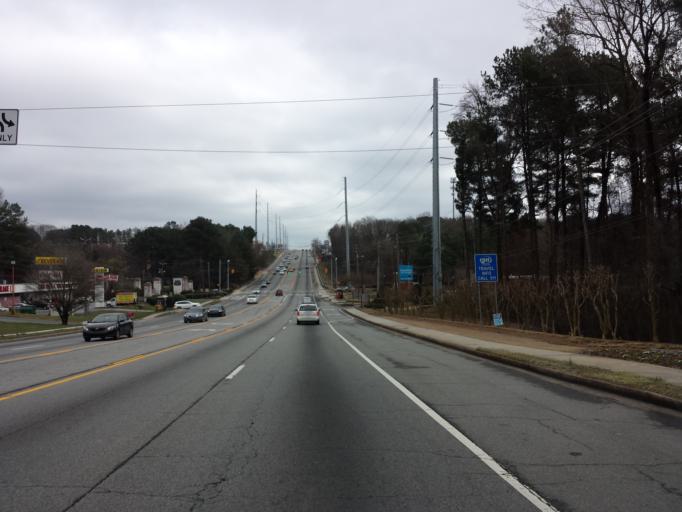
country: US
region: Georgia
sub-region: Cobb County
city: Smyrna
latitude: 33.8961
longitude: -84.4812
